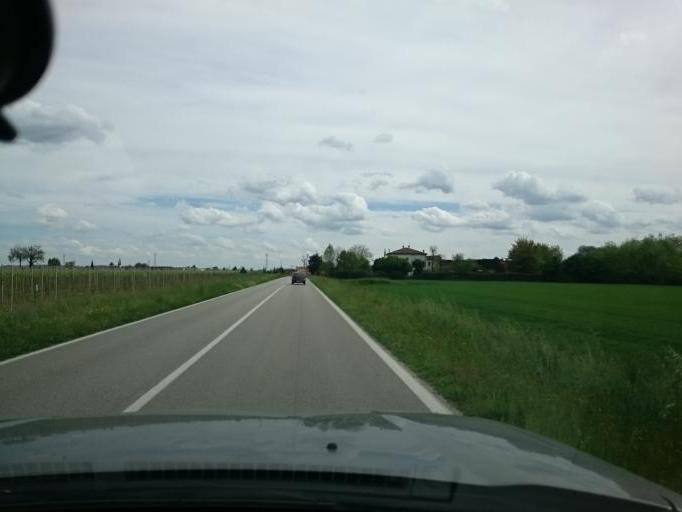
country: IT
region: Veneto
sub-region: Provincia di Vicenza
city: Longare
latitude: 45.4762
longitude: 11.6223
